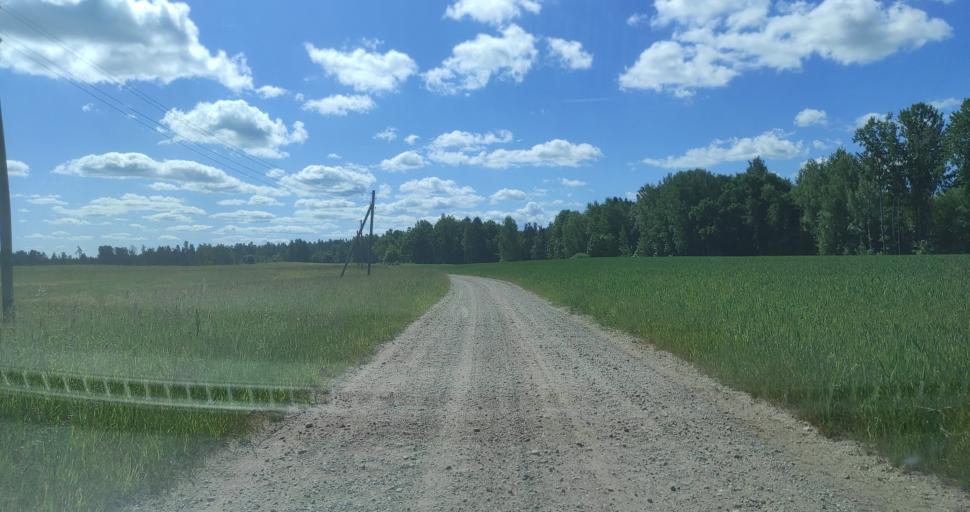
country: LV
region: Alsunga
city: Alsunga
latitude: 56.8958
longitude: 21.7121
